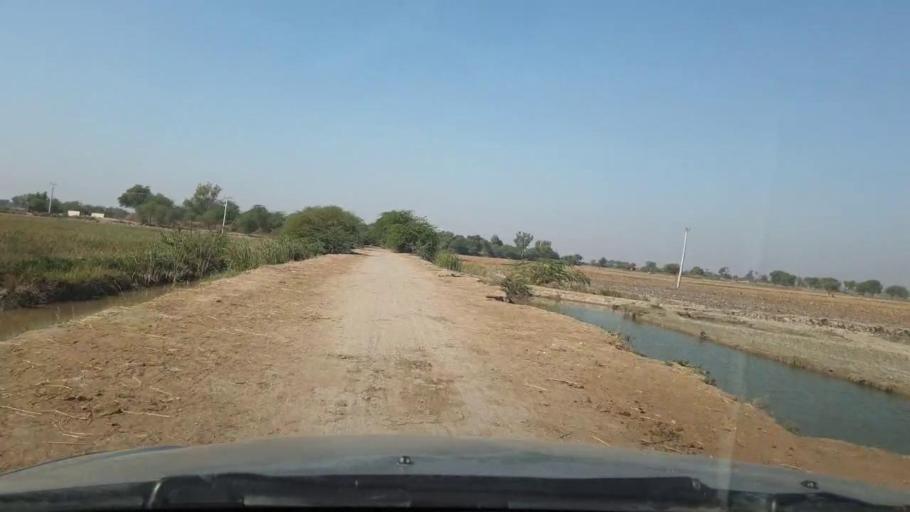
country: PK
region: Sindh
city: Kario
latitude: 24.8929
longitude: 68.5616
